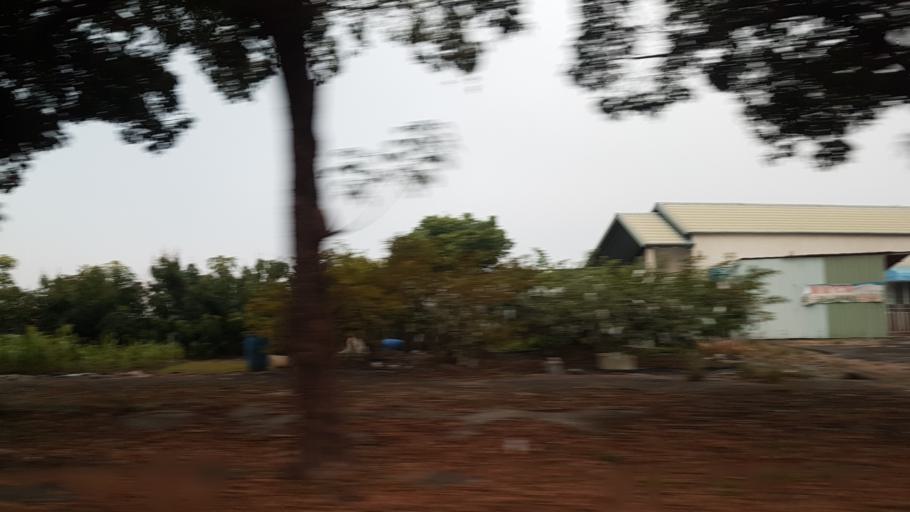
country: TW
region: Taiwan
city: Xinying
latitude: 23.3553
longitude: 120.4166
